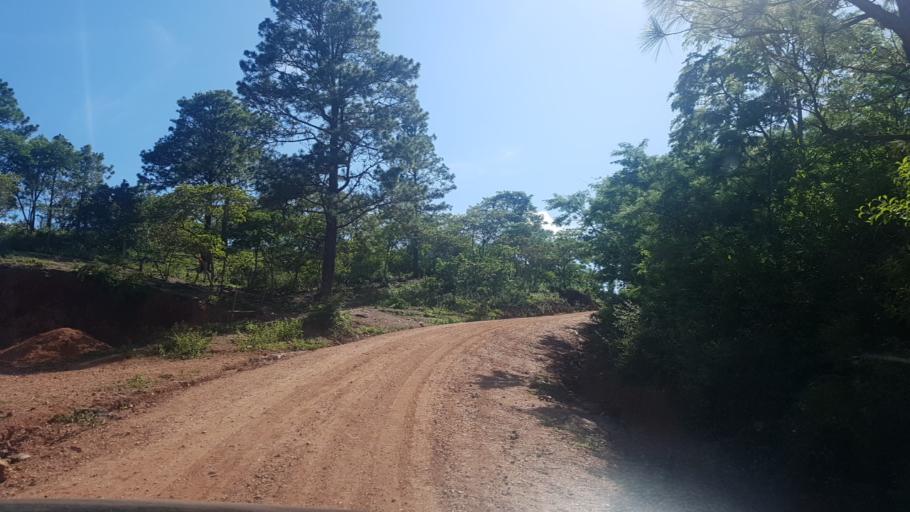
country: NI
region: Nueva Segovia
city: Ocotal
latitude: 13.6430
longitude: -86.6165
